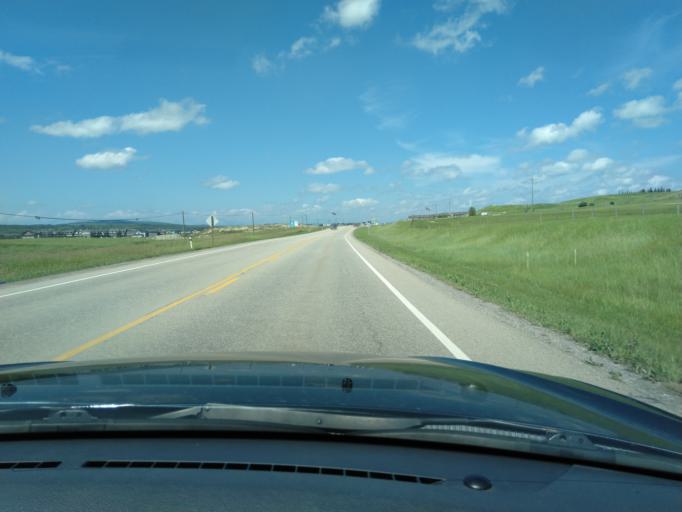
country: CA
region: Alberta
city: Cochrane
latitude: 51.2011
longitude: -114.4943
